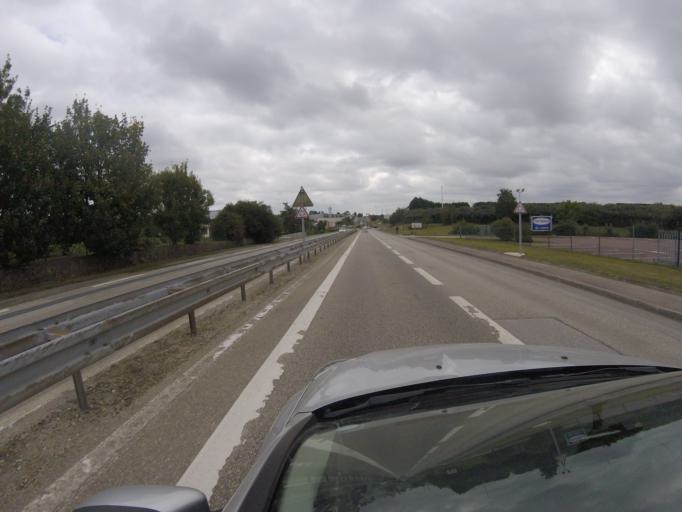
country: FR
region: Lower Normandy
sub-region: Departement de la Manche
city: La Glacerie
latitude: 49.6070
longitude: -1.5995
